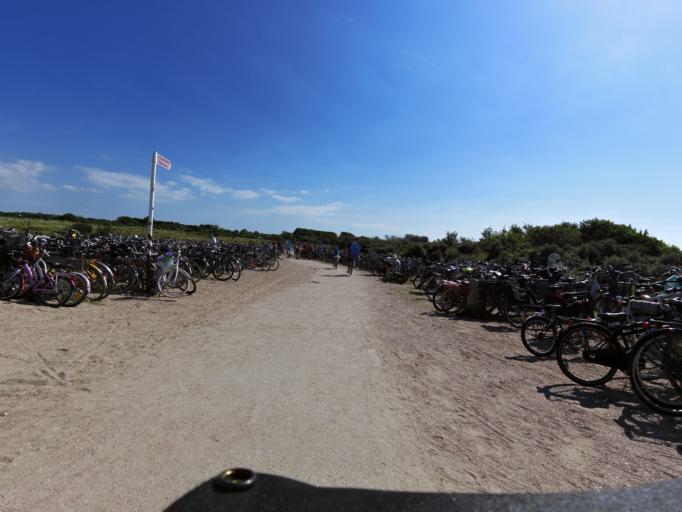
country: NL
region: Zeeland
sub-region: Schouwen-Duiveland
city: Renesse
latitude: 51.7369
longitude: 3.7520
